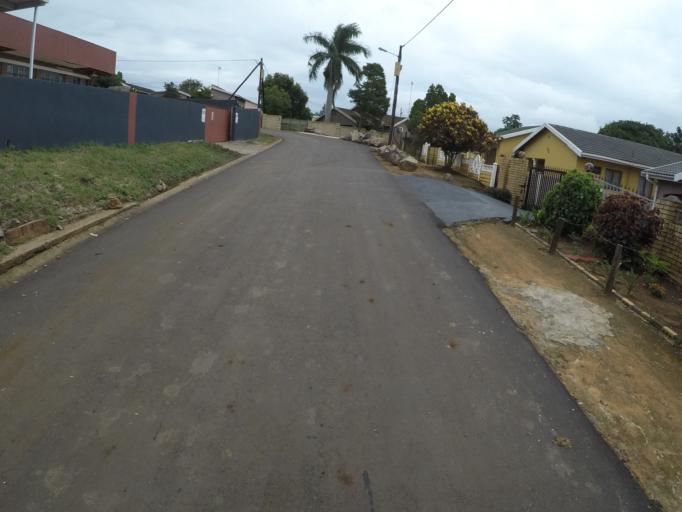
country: ZA
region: KwaZulu-Natal
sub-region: uThungulu District Municipality
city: Empangeni
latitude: -28.7754
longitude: 31.8521
